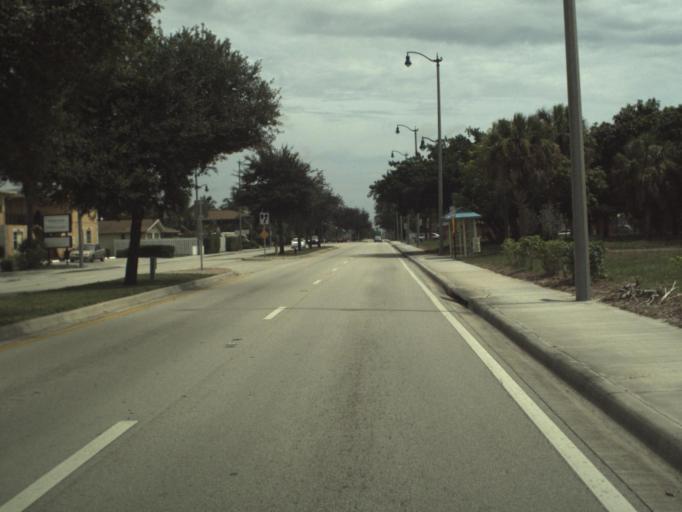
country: US
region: Florida
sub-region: Palm Beach County
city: Mangonia Park
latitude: 26.7412
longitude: -80.0566
